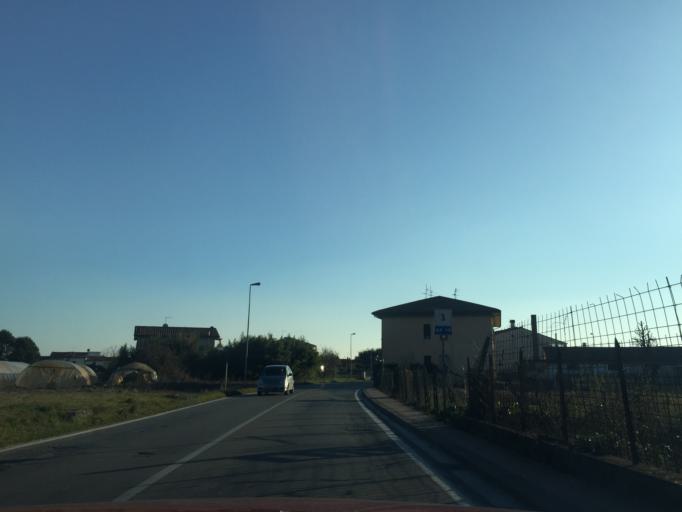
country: IT
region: Tuscany
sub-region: Provincia di Pistoia
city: Ponte Buggianese
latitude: 43.8508
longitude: 10.7466
